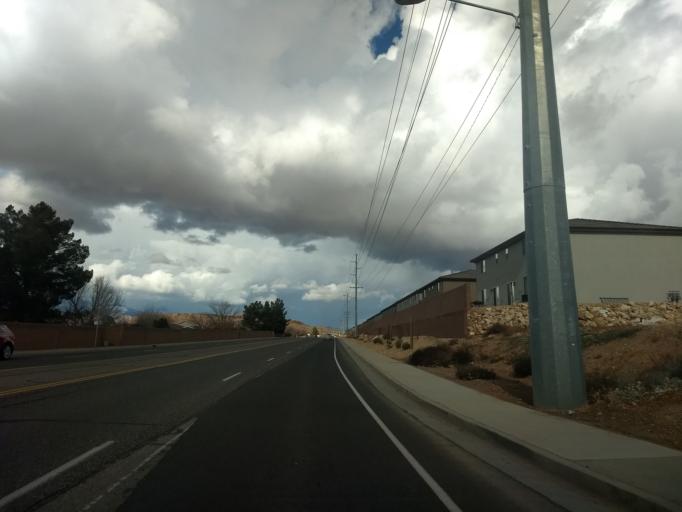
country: US
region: Utah
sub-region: Washington County
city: Saint George
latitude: 37.0525
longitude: -113.5548
